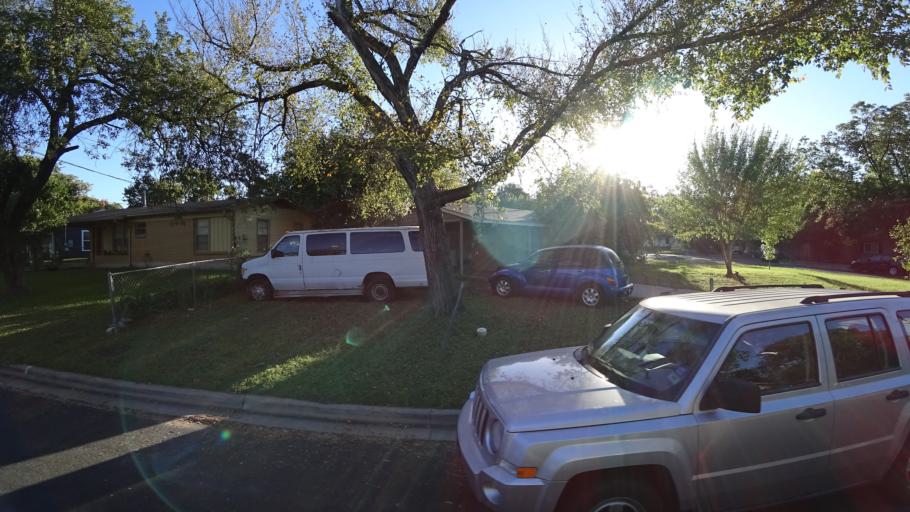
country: US
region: Texas
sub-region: Travis County
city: Austin
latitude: 30.2997
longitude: -97.6845
